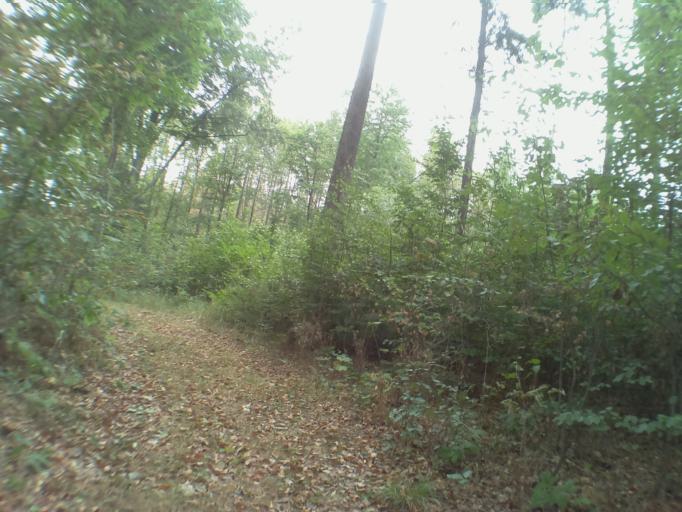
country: PL
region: Lower Silesian Voivodeship
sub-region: Powiat swidnicki
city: Strzegom
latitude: 50.9896
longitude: 16.3097
